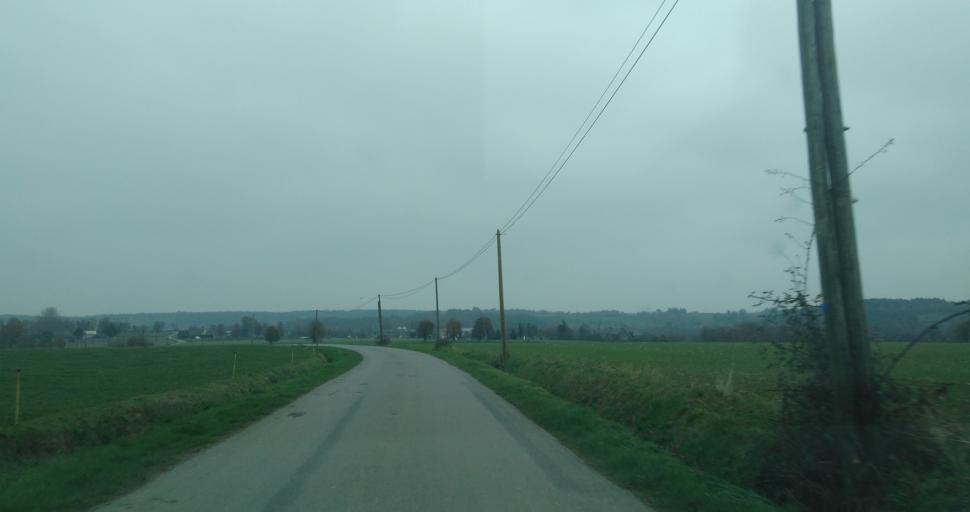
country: FR
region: Brittany
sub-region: Departement d'Ille-et-Vilaine
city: Iffendic
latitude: 48.0943
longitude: -2.0864
